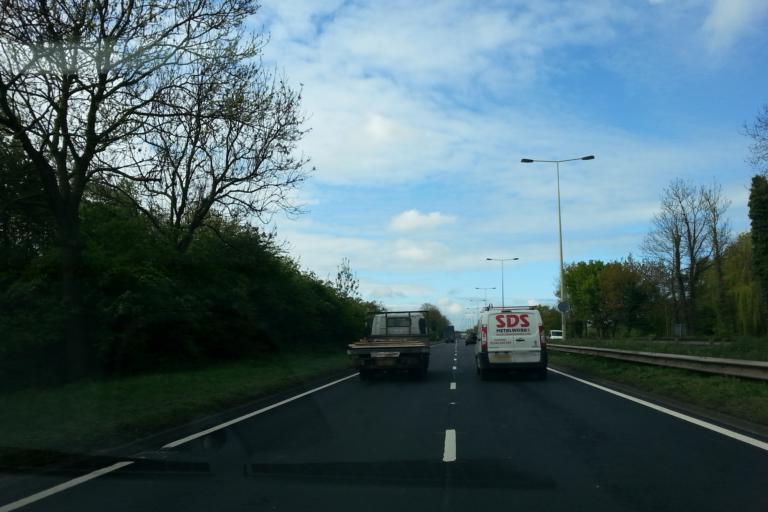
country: GB
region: England
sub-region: Staffordshire
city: Barton under Needwood
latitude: 52.7521
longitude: -1.7141
